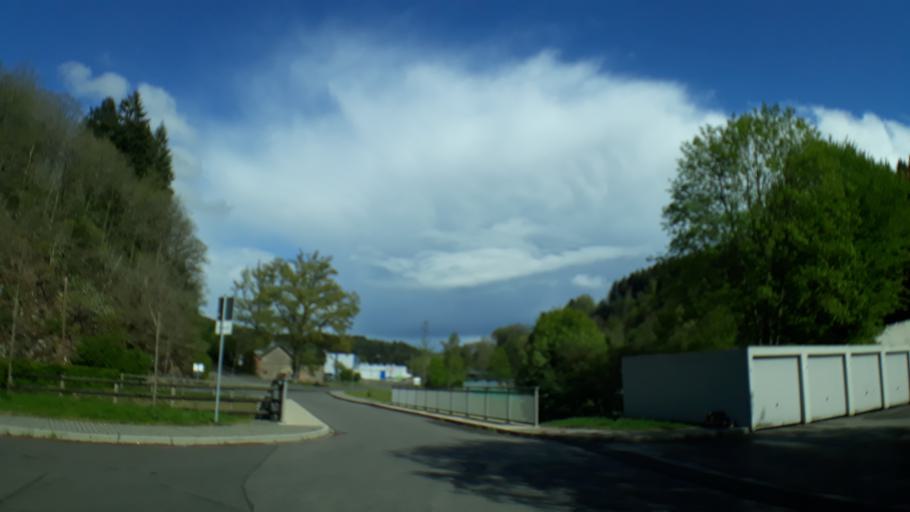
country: DE
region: North Rhine-Westphalia
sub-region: Regierungsbezirk Koln
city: Hellenthal
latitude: 50.4936
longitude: 6.4234
